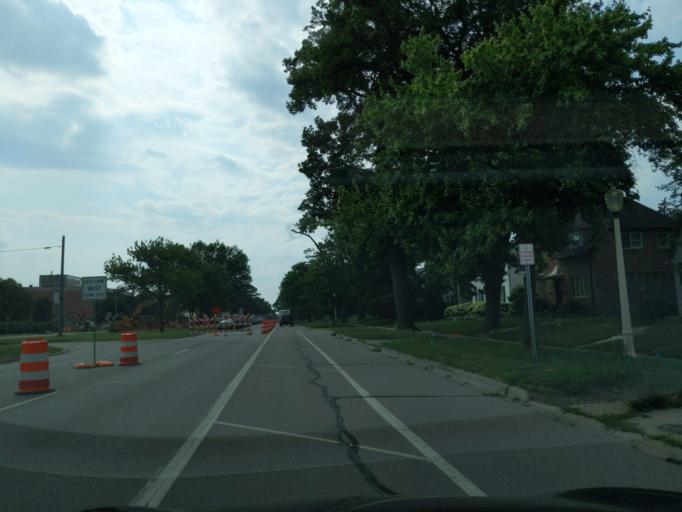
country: US
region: Michigan
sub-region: Ingham County
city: East Lansing
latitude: 42.7336
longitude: -84.4958
